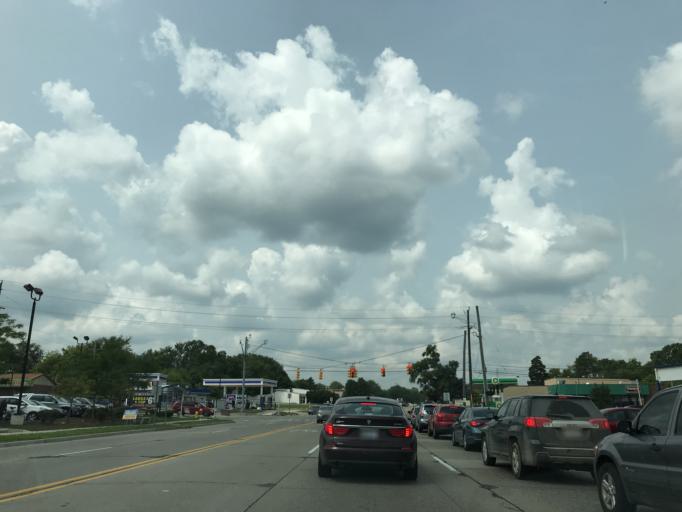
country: US
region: Michigan
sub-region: Washtenaw County
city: Ypsilanti
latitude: 42.2500
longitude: -83.6600
